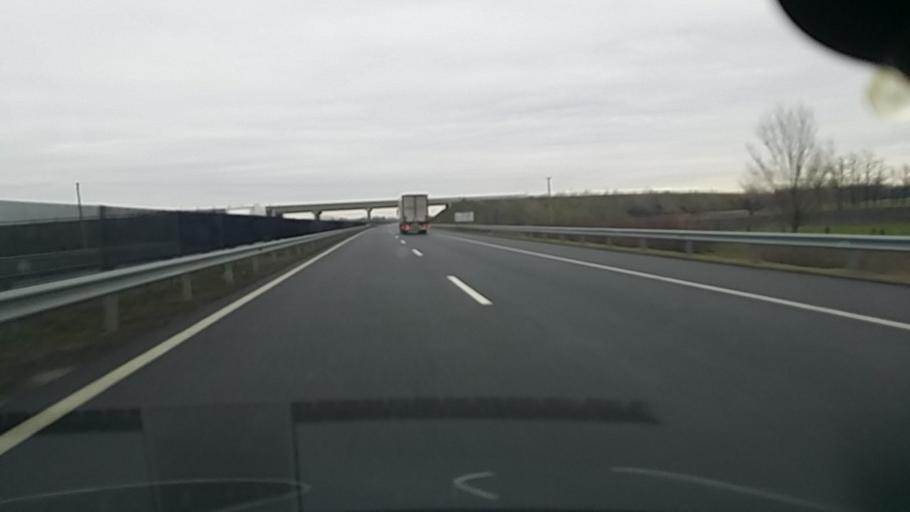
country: HU
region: Hajdu-Bihar
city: Hajdunanas
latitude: 47.8605
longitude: 21.3615
